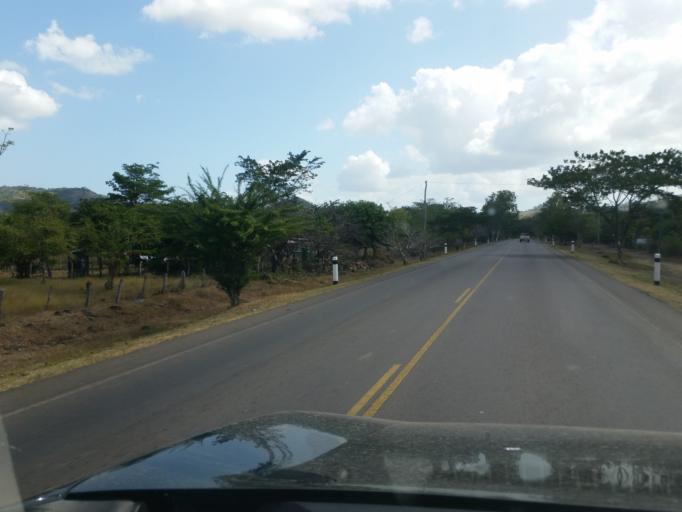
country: NI
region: Chontales
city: Comalapa
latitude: 12.1939
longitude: -85.6182
